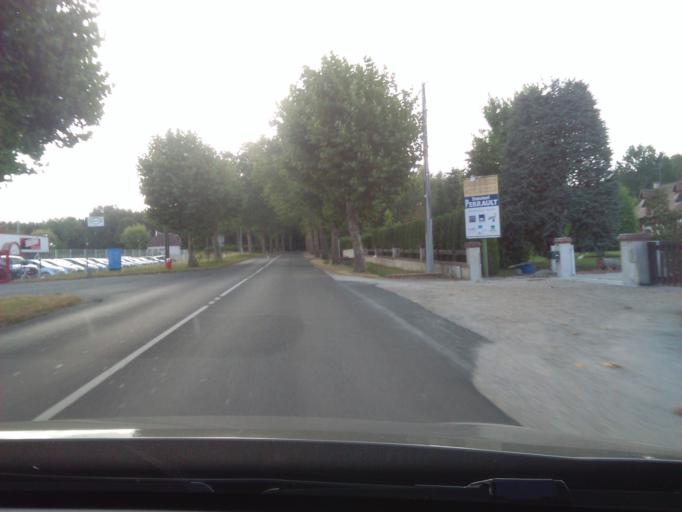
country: FR
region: Centre
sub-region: Departement du Loir-et-Cher
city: Cellettes
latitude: 47.5206
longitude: 1.3930
